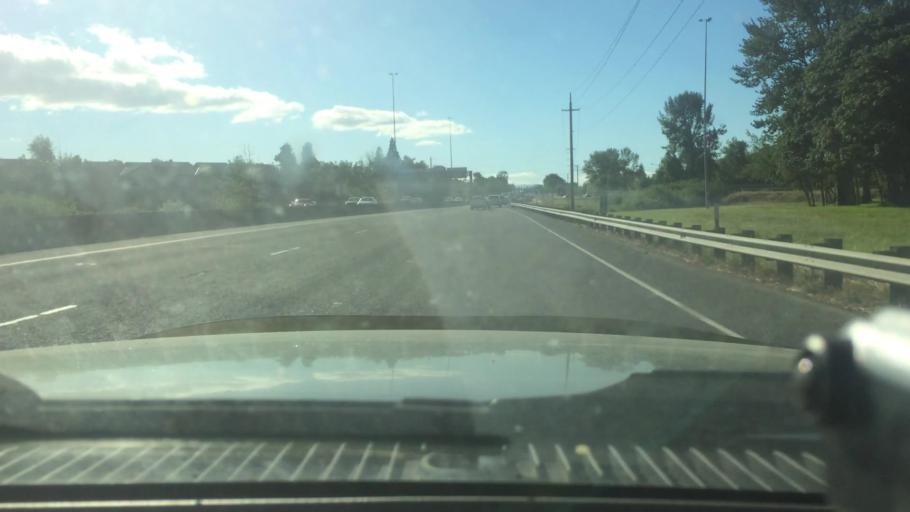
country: US
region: Oregon
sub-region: Lane County
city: Eugene
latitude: 44.0918
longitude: -123.0998
